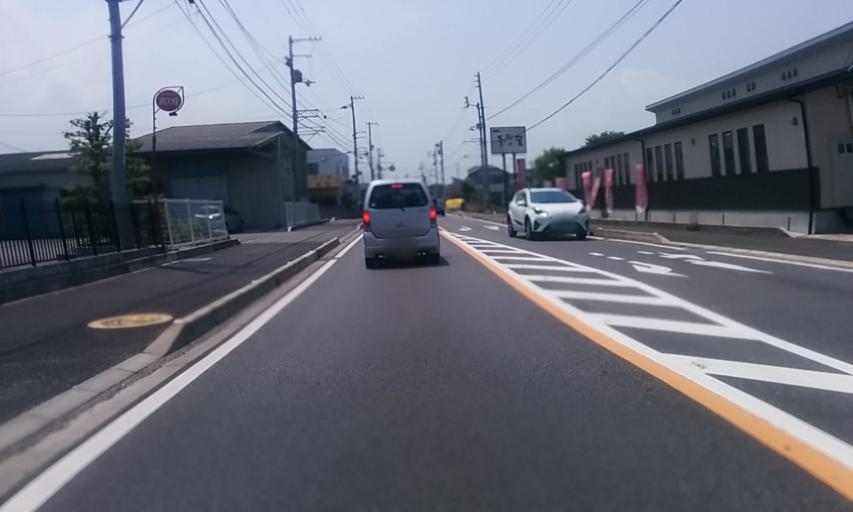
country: JP
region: Ehime
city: Saijo
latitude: 33.9075
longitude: 133.1897
